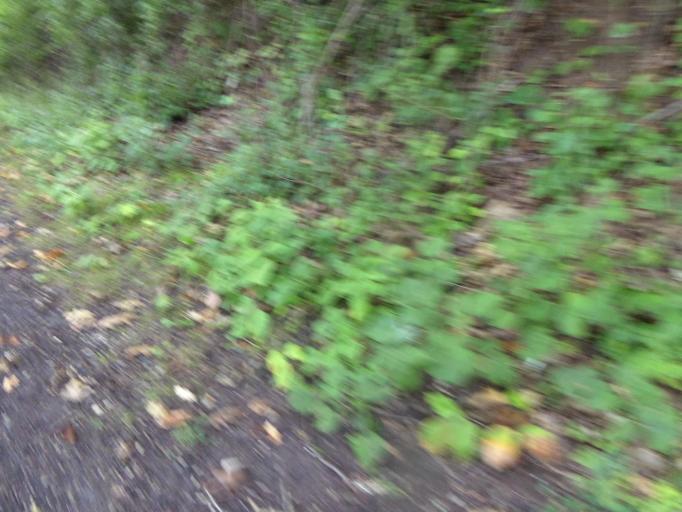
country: US
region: Minnesota
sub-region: Washington County
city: Afton
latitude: 44.8537
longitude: -92.7726
